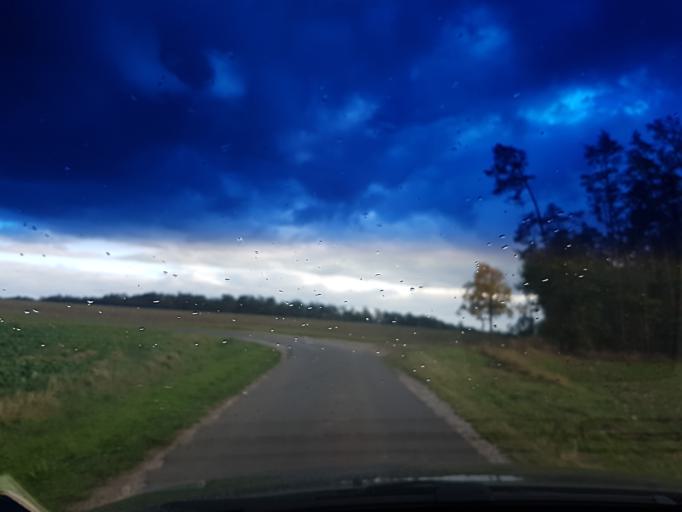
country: DE
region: Bavaria
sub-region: Regierungsbezirk Mittelfranken
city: Burghaslach
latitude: 49.7475
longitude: 10.5815
